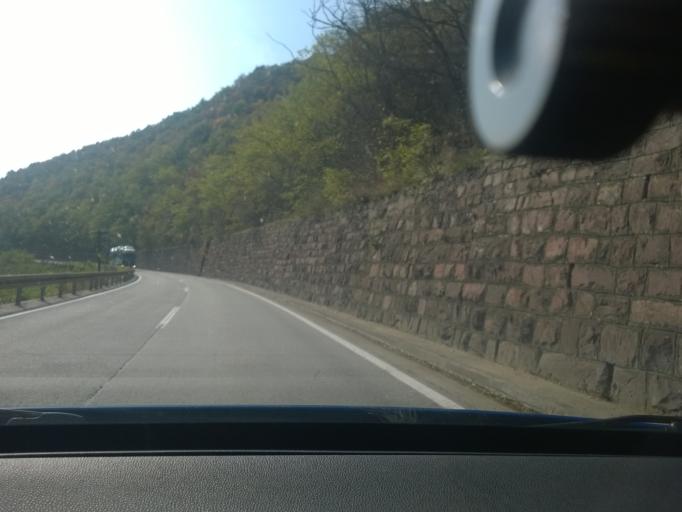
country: RS
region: Central Serbia
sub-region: Nisavski Okrug
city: Niska Banja
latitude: 43.3213
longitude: 22.0502
